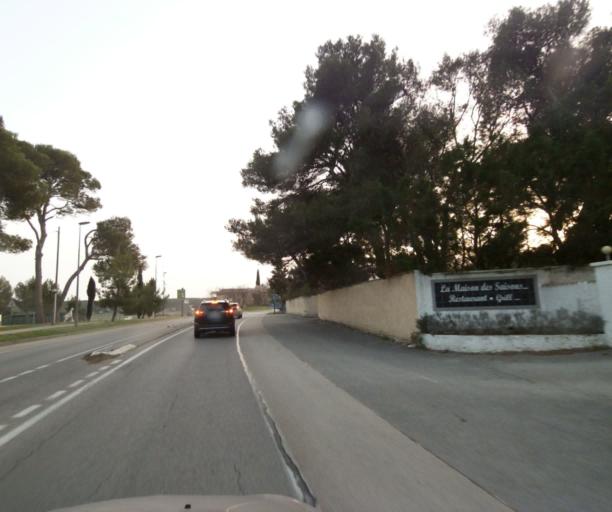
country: FR
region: Provence-Alpes-Cote d'Azur
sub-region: Departement des Bouches-du-Rhone
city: Cabries
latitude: 43.4467
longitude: 5.3611
